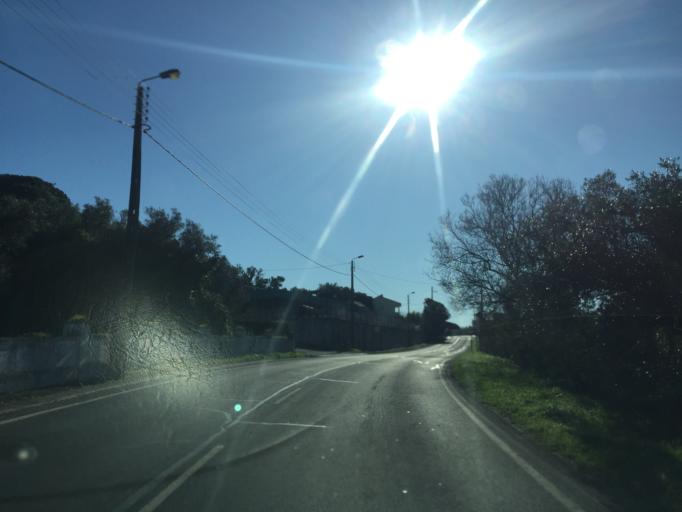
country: PT
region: Lisbon
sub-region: Sintra
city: Pero Pinheiro
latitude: 38.8364
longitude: -9.3101
